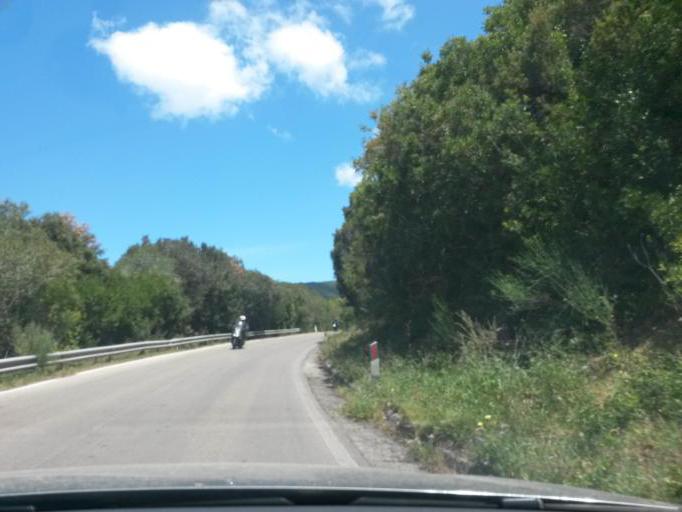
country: IT
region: Tuscany
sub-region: Provincia di Livorno
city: Campo nell'Elba
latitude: 42.7569
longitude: 10.2496
